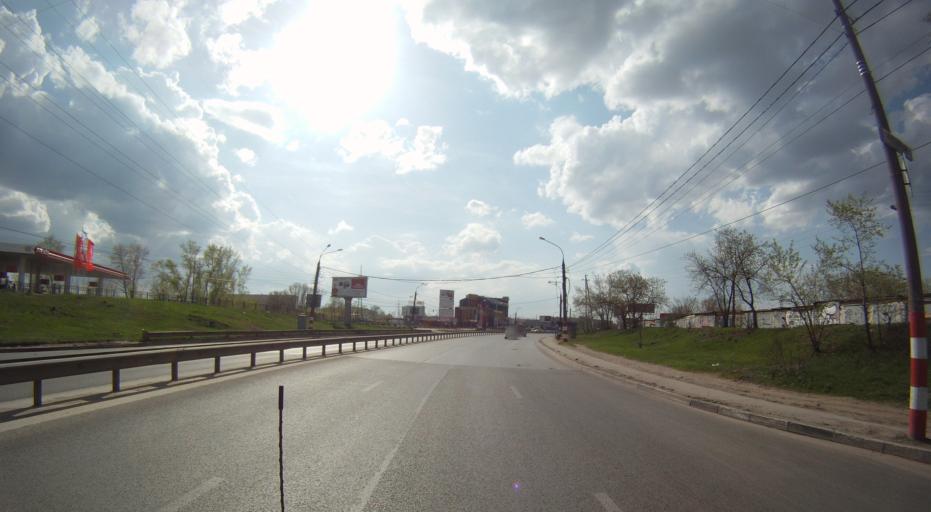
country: RU
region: Nizjnij Novgorod
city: Nizhniy Novgorod
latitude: 56.2963
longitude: 43.9333
